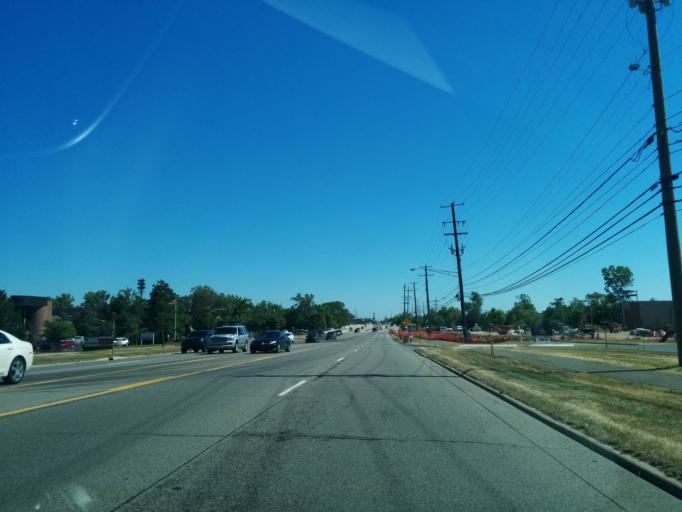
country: US
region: Michigan
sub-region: Oakland County
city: West Bloomfield Township
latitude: 42.5352
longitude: -83.3605
